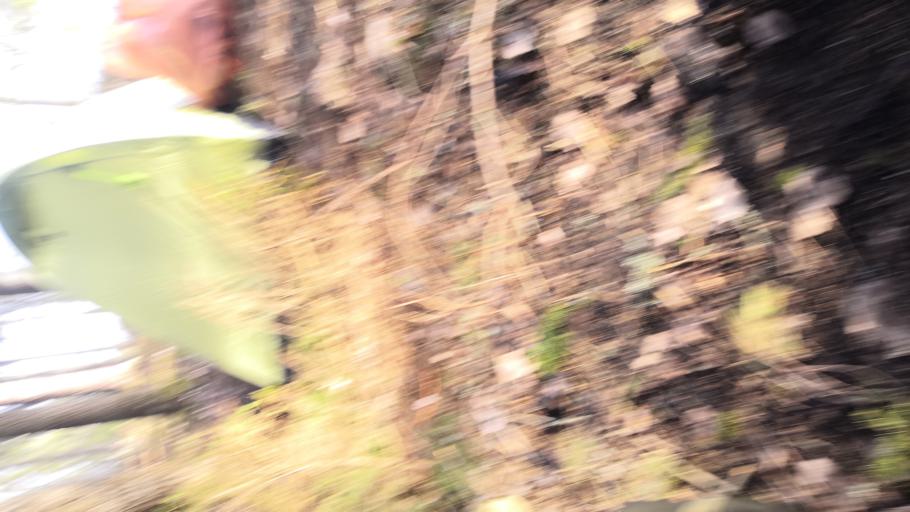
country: RU
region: Leningrad
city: Veshchevo
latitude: 60.5460
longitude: 29.2822
